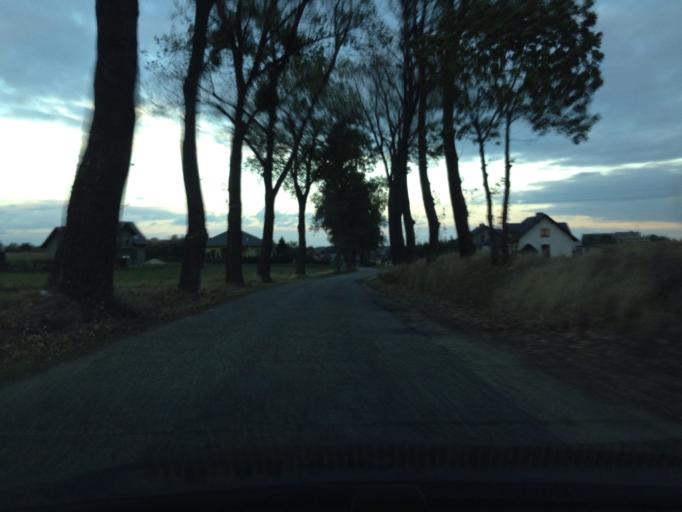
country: PL
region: Kujawsko-Pomorskie
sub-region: Powiat brodnicki
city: Gorzno
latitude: 53.1960
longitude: 19.6283
